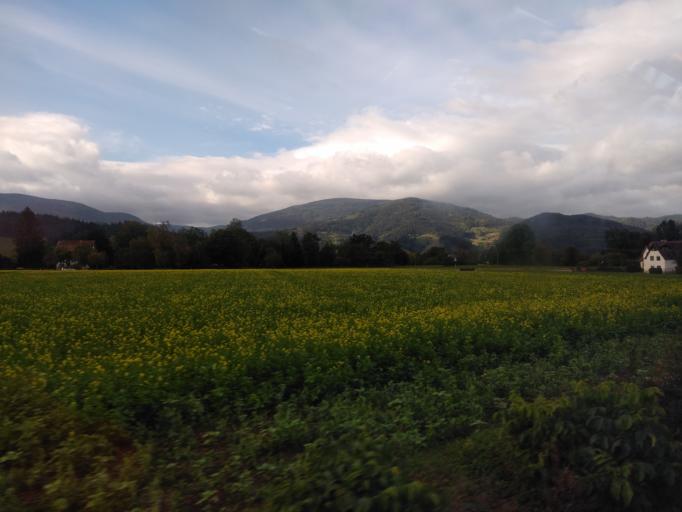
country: DE
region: Baden-Wuerttemberg
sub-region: Freiburg Region
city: Stegen
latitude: 47.9683
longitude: 7.9723
